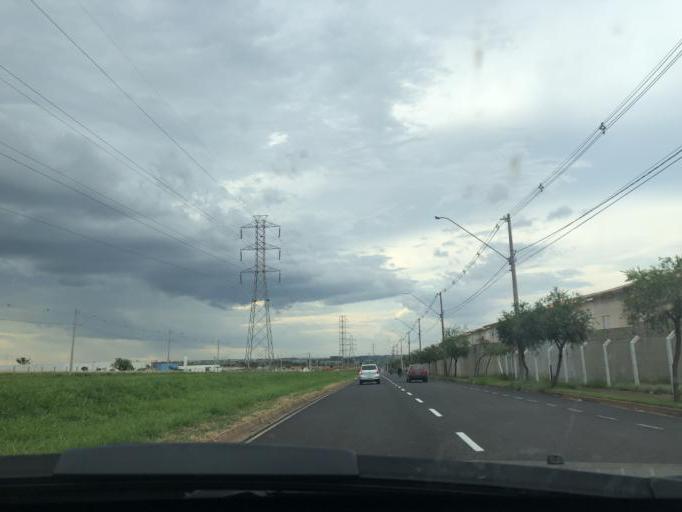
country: BR
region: Sao Paulo
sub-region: Sao Jose Do Rio Preto
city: Sao Jose do Rio Preto
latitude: -20.8396
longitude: -49.4173
